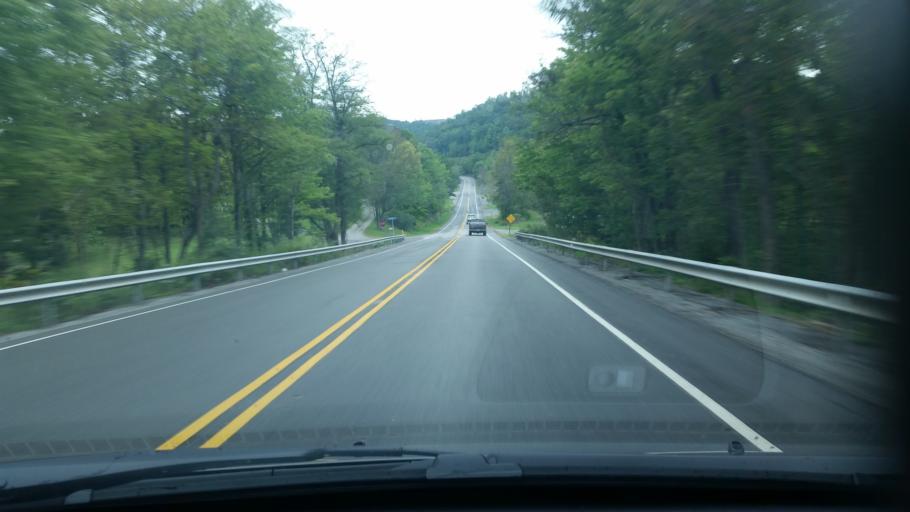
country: US
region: Pennsylvania
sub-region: Clearfield County
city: Shiloh
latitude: 41.0713
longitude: -78.3247
